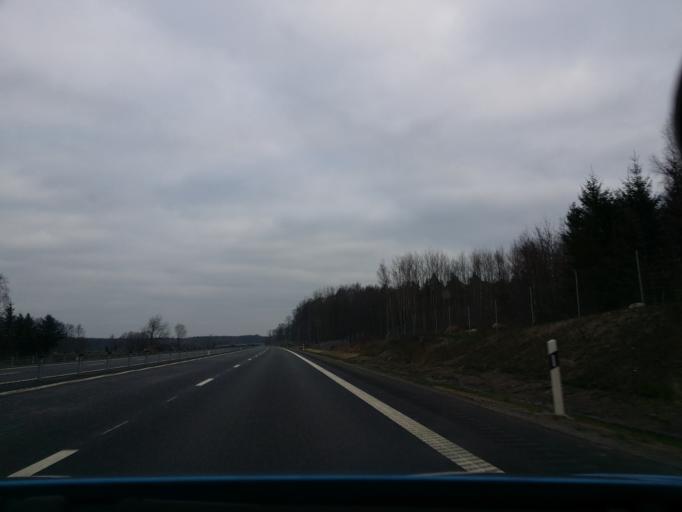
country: SE
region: Blekinge
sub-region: Karlshamns Kommun
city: Morrum
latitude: 56.1425
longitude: 14.6625
